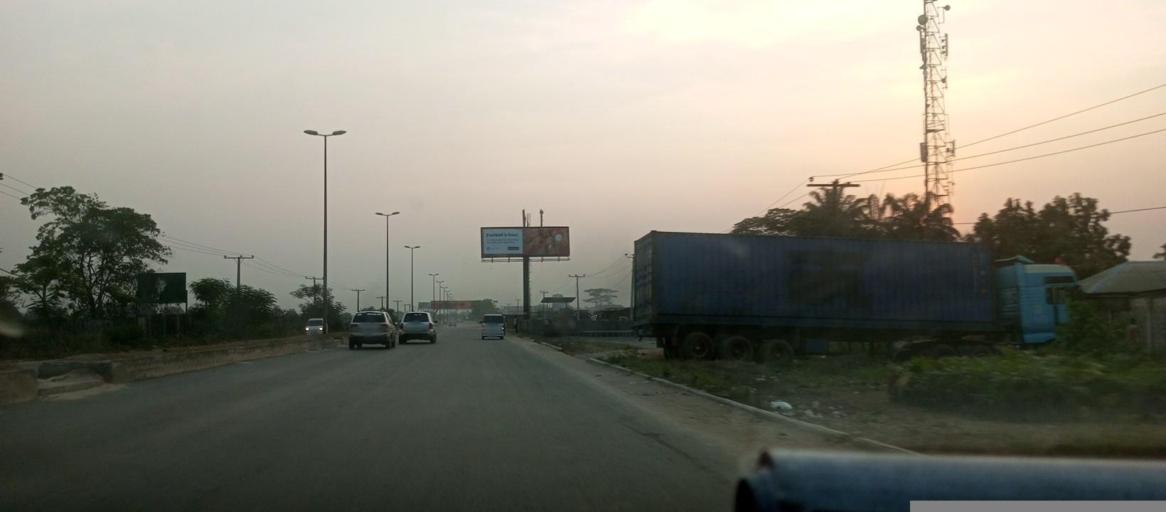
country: NG
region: Rivers
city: Emuoha
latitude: 4.9323
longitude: 7.0032
